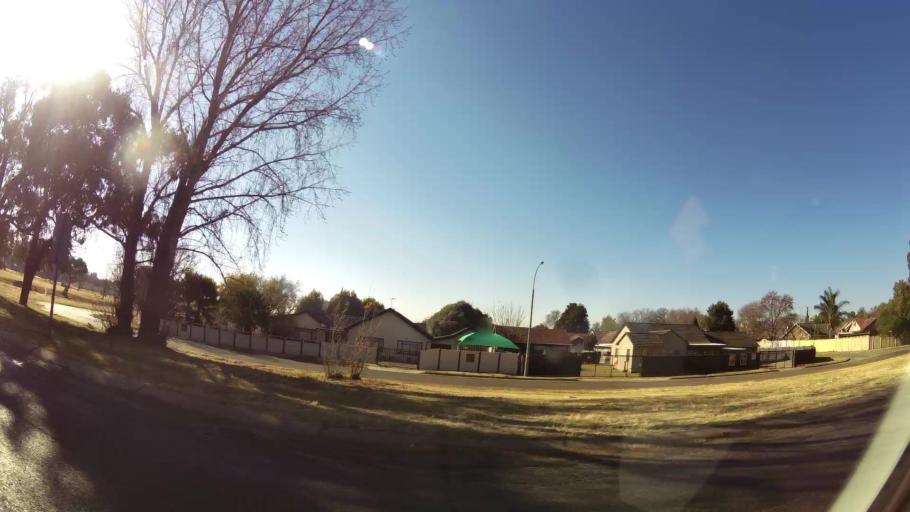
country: ZA
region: Gauteng
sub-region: Ekurhuleni Metropolitan Municipality
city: Germiston
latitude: -26.2940
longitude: 28.1188
